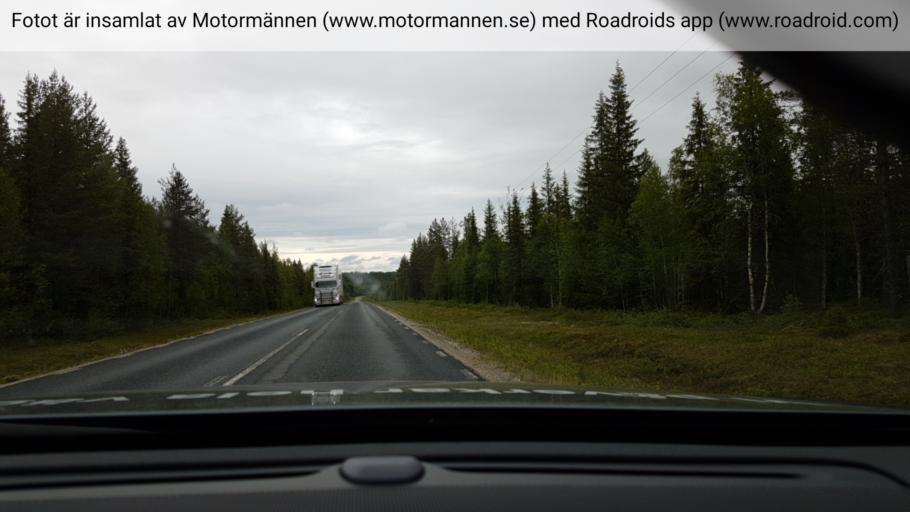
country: SE
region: Vaesterbotten
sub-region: Lycksele Kommun
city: Soderfors
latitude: 64.4657
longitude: 18.1675
